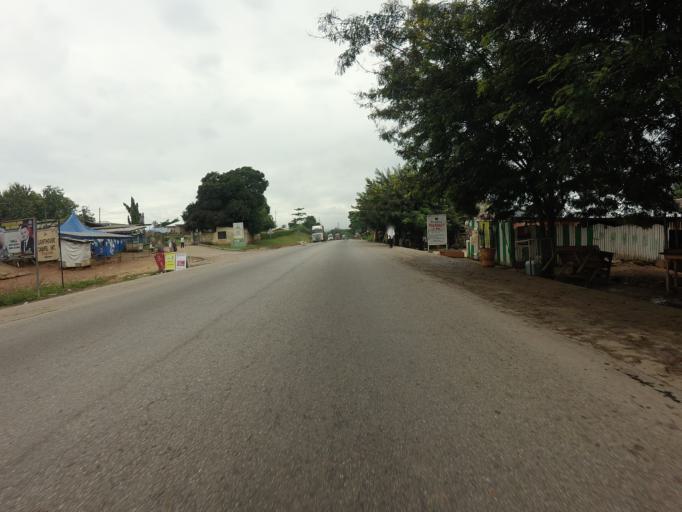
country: GH
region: Eastern
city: Nkawkaw
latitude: 6.4366
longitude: -0.5860
